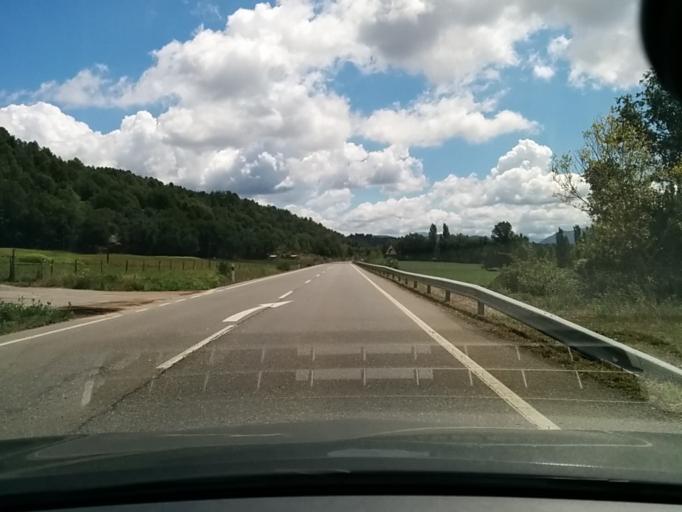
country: ES
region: Aragon
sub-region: Provincia de Huesca
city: Labuerda
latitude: 42.4328
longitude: 0.1044
